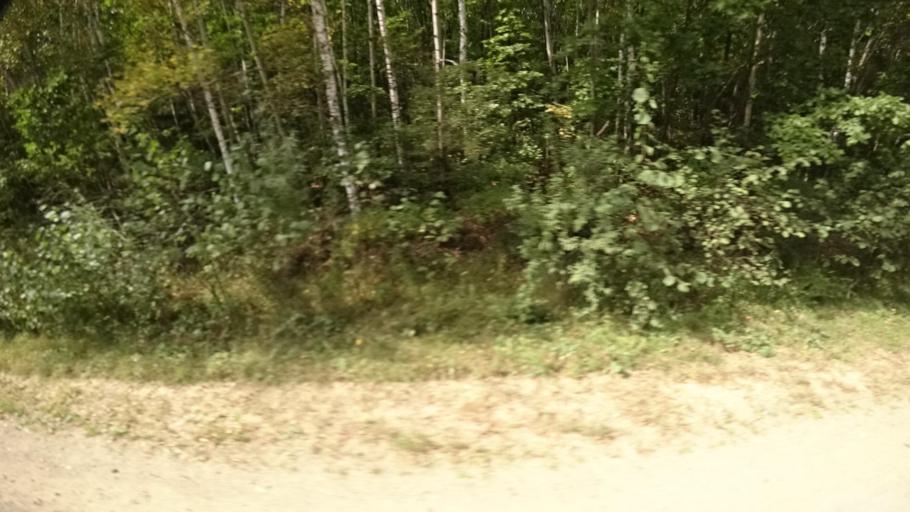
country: RU
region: Primorskiy
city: Yakovlevka
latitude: 44.6730
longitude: 133.6118
